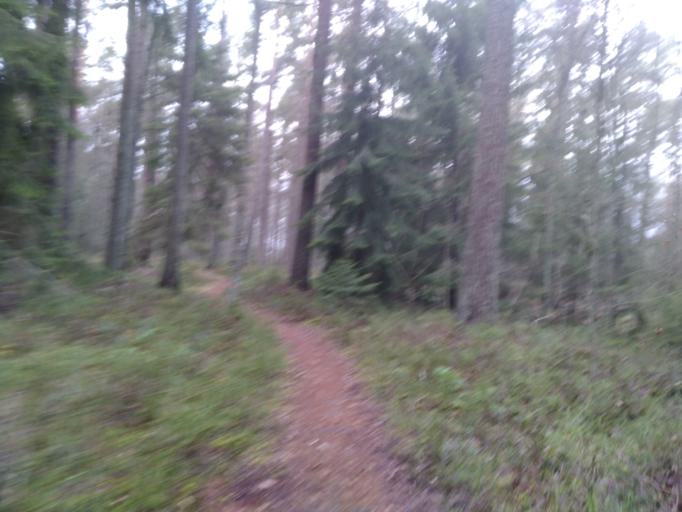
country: SE
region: Vaestra Goetaland
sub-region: Lidkopings Kommun
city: Lidkoping
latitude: 58.4871
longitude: 13.1565
